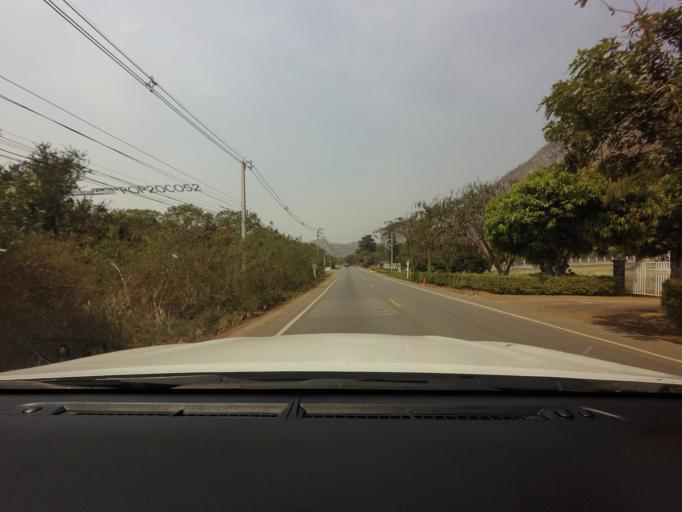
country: TH
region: Sara Buri
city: Muak Lek
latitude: 14.5840
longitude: 101.2532
